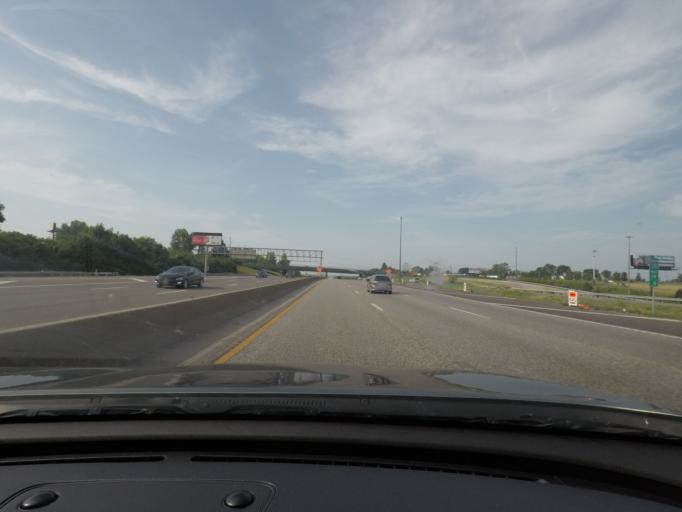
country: US
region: Missouri
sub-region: Saint Louis County
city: Maryland Heights
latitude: 38.7444
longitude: -90.4406
